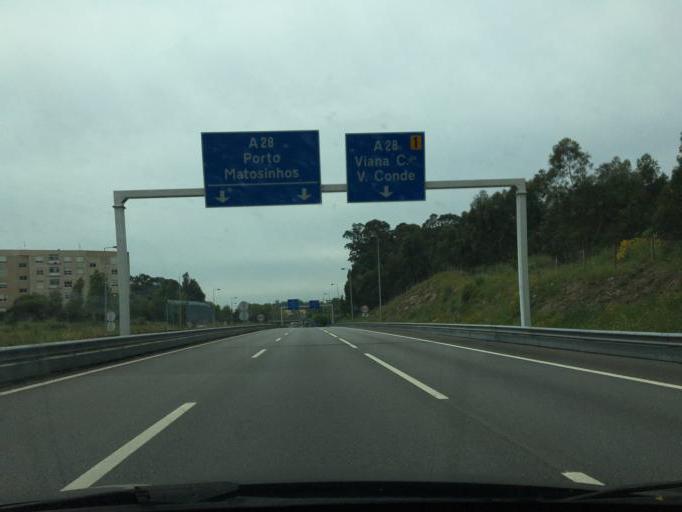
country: PT
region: Porto
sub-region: Matosinhos
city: Santa Cruz do Bispo
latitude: 41.2323
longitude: -8.6907
